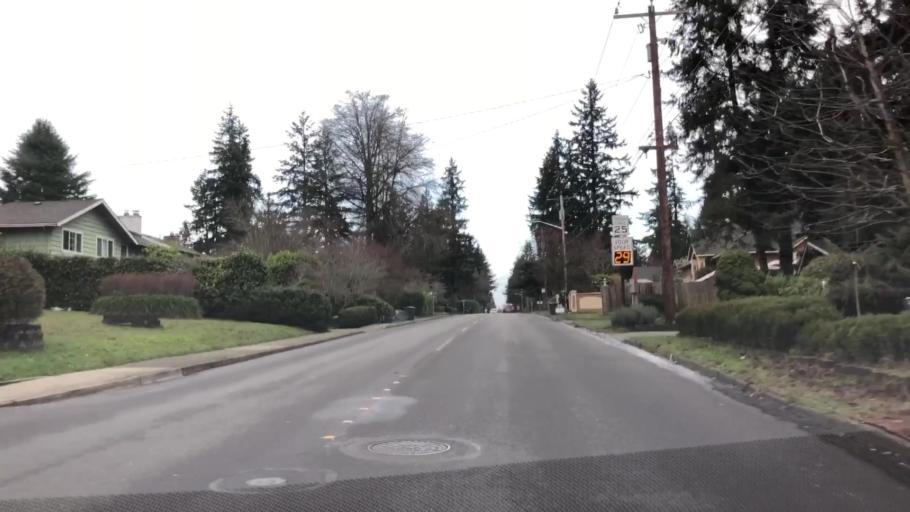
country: US
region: Washington
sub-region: King County
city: West Lake Sammamish
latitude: 47.6108
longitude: -122.1213
